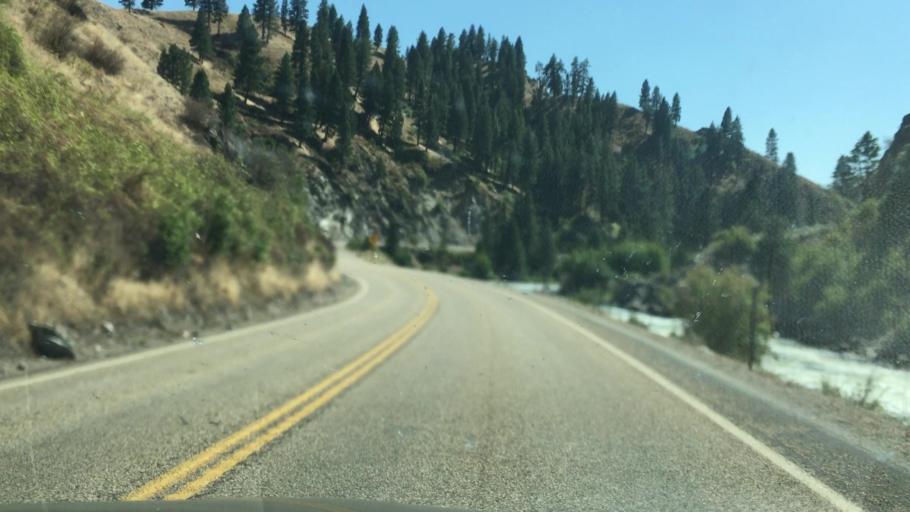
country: US
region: Idaho
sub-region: Boise County
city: Idaho City
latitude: 44.1020
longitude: -116.0950
